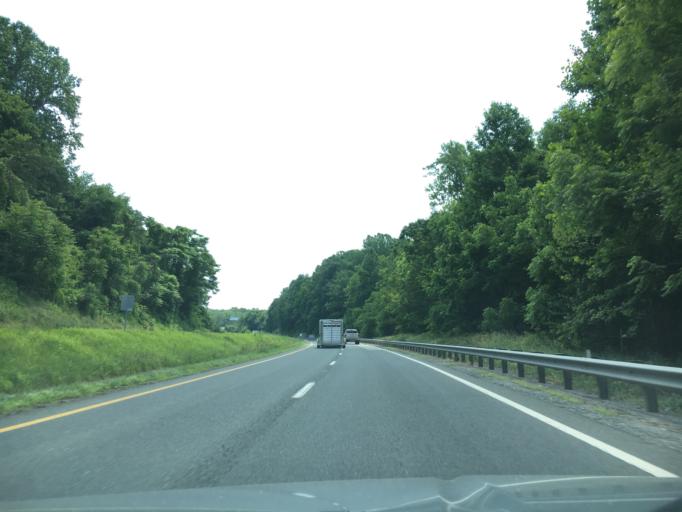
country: US
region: Virginia
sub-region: Campbell County
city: Concord
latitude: 37.3752
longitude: -79.0404
